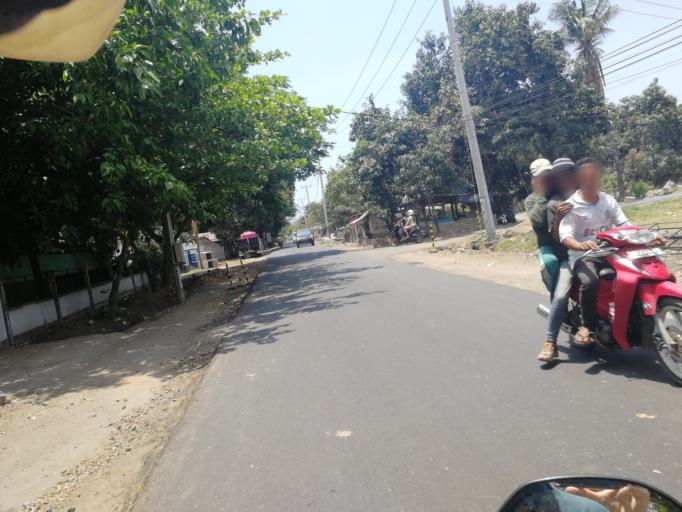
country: ID
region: West Nusa Tenggara
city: Pemenang
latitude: -8.4006
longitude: 116.1014
